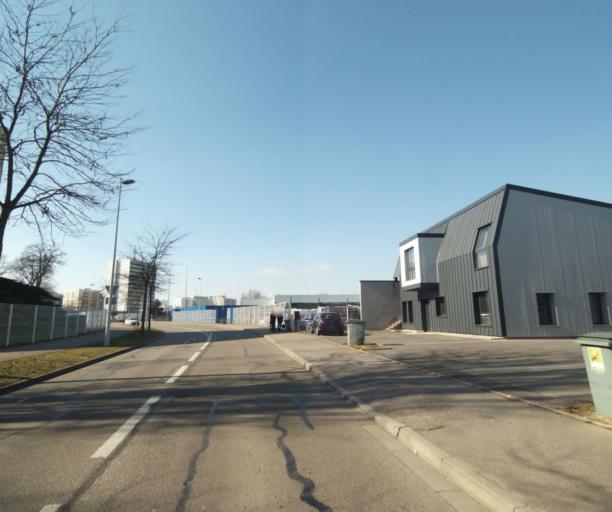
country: FR
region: Lorraine
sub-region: Departement de Meurthe-et-Moselle
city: Vandoeuvre-les-Nancy
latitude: 48.6612
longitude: 6.1900
